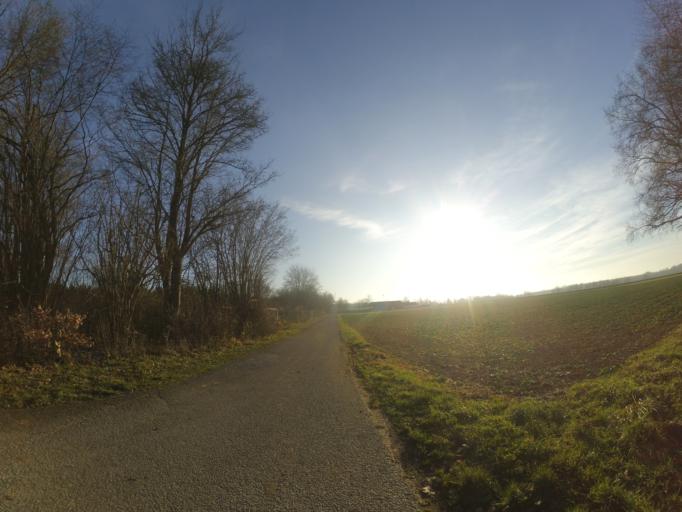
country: DE
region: Baden-Wuerttemberg
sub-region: Tuebingen Region
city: Dornstadt
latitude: 48.4386
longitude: 9.8975
